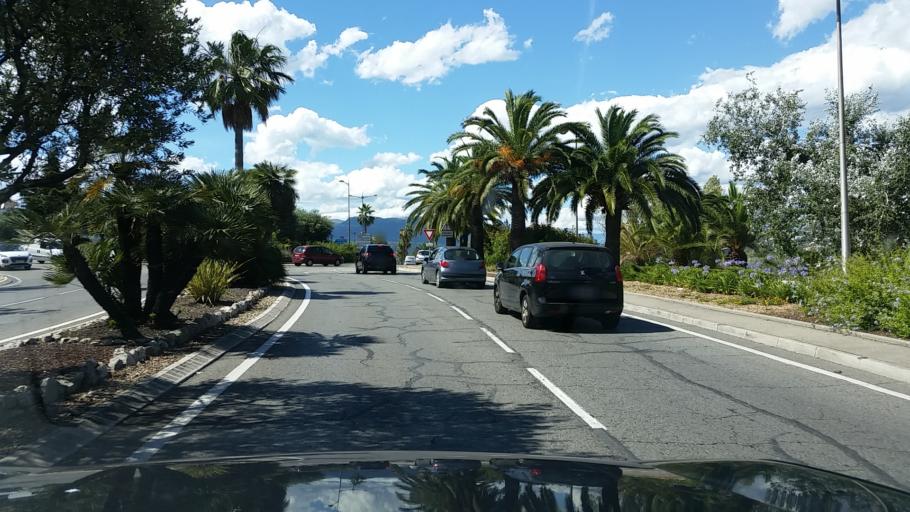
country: FR
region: Provence-Alpes-Cote d'Azur
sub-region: Departement des Alpes-Maritimes
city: Saint-Laurent-du-Var
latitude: 43.6680
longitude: 7.1958
